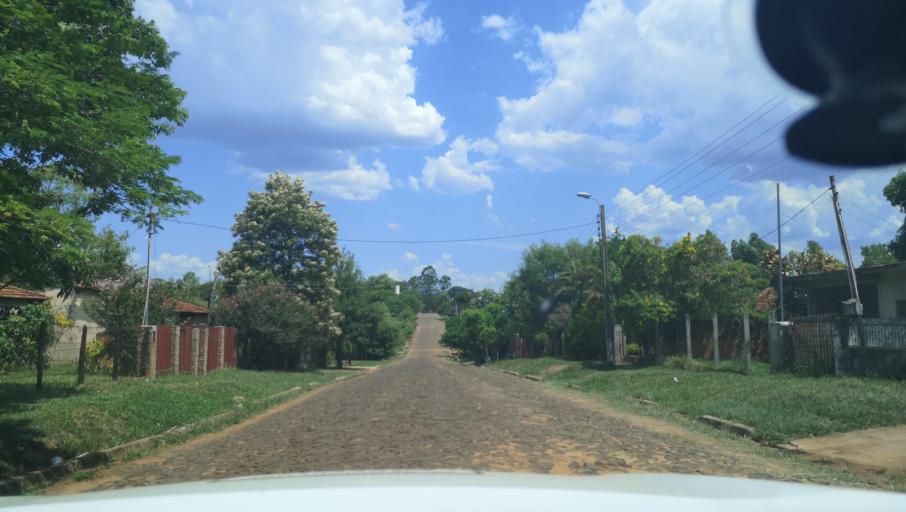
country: PY
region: Itapua
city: Carmen del Parana
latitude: -27.1696
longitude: -56.2451
